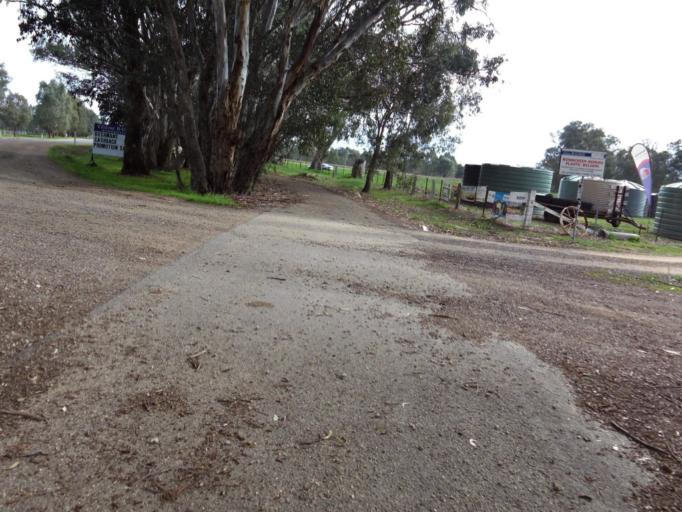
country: AU
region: Victoria
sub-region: Wangaratta
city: Wangaratta
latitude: -36.3967
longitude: 146.3444
